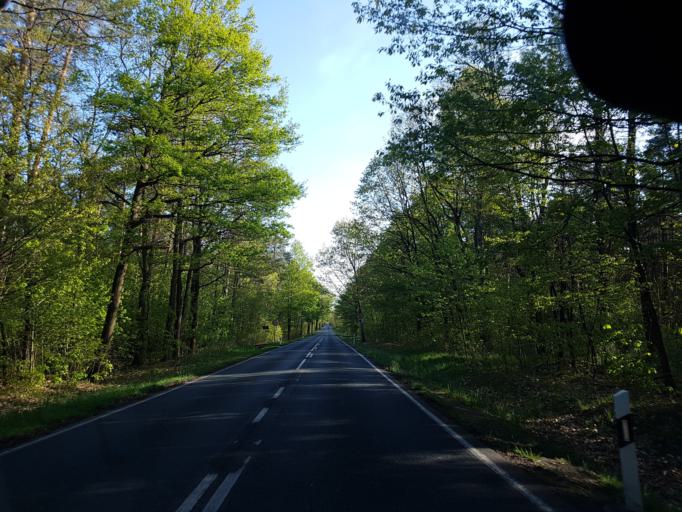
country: DE
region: Brandenburg
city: Altdobern
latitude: 51.6285
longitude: 14.0282
